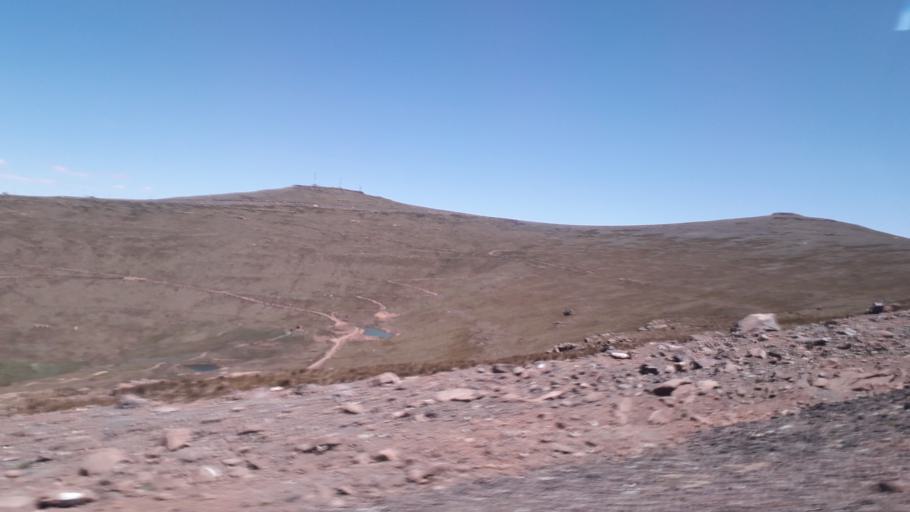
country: ZA
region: Orange Free State
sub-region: Thabo Mofutsanyana District Municipality
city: Phuthaditjhaba
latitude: -28.8219
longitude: 28.7335
